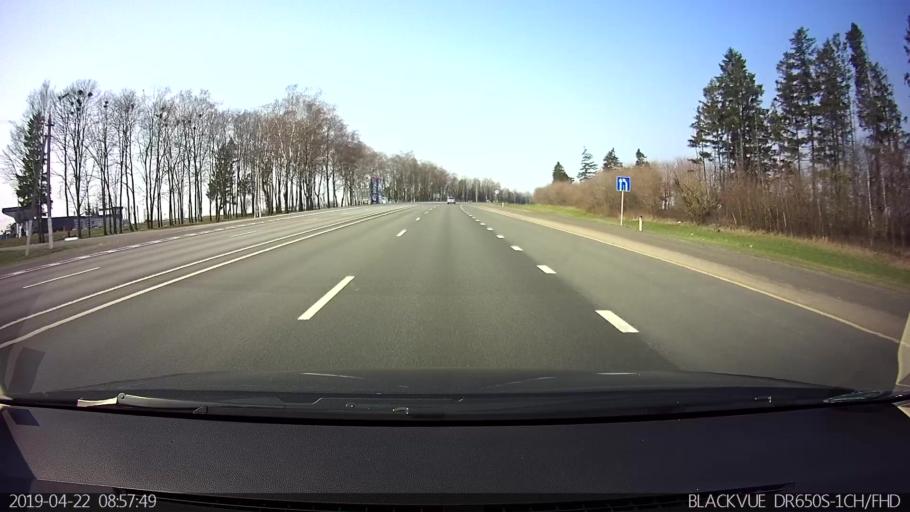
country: RU
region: Smolensk
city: Pechersk
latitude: 54.8663
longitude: 32.0086
